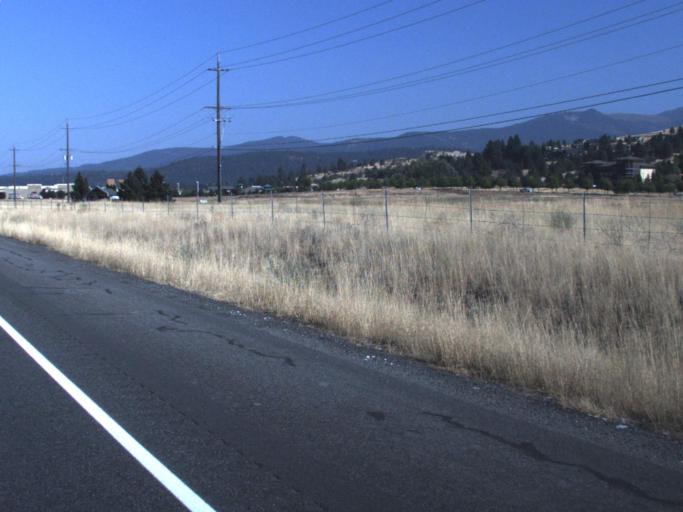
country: US
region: Washington
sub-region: Spokane County
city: Liberty Lake
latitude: 47.6669
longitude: -117.1242
